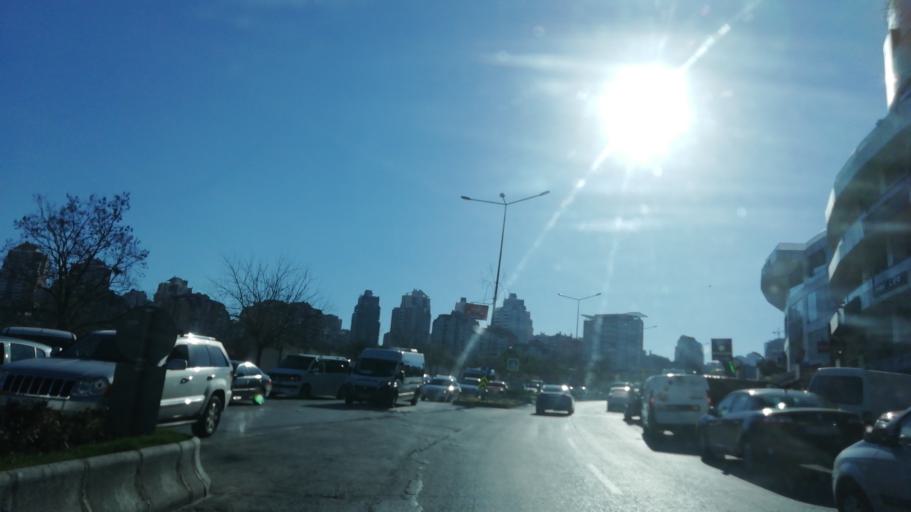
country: TR
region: Istanbul
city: Esenyurt
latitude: 41.0706
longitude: 28.6878
